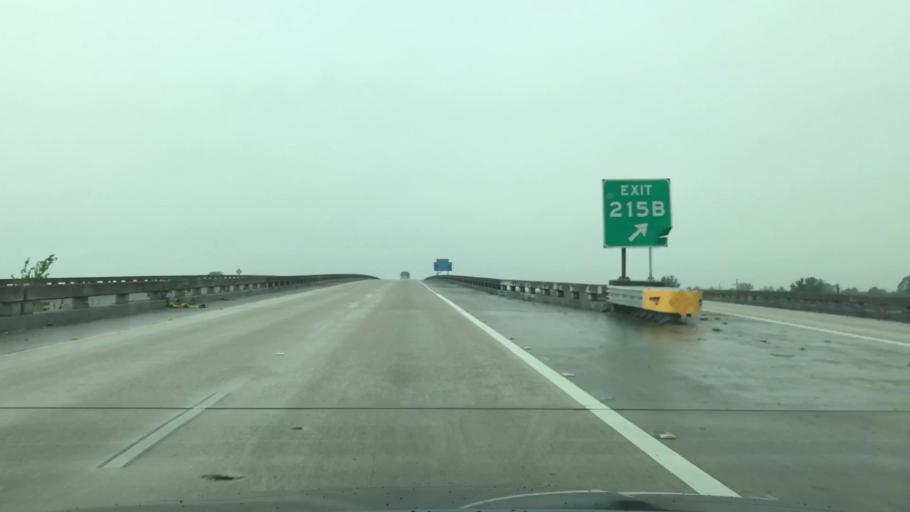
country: US
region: Louisiana
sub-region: Lafourche Parish
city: Mathews
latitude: 29.7109
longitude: -90.5694
